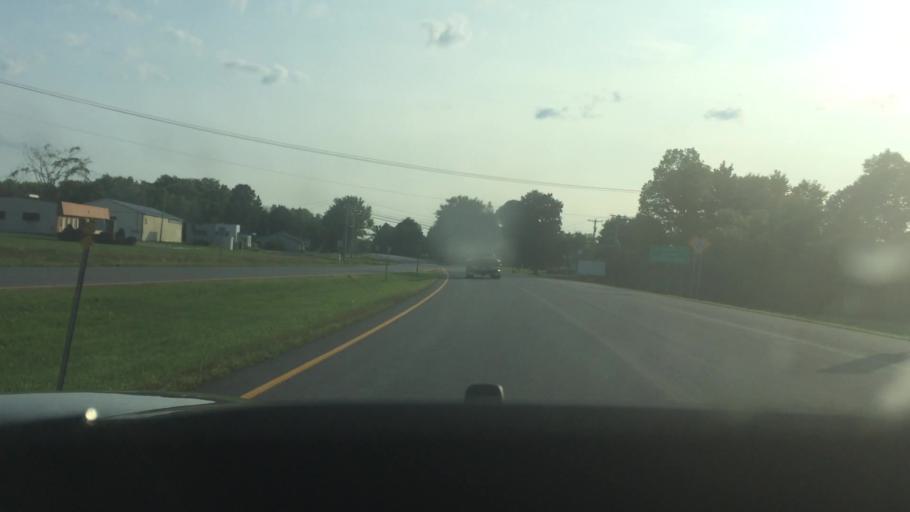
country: US
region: New York
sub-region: St. Lawrence County
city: Ogdensburg
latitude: 44.6787
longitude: -75.5203
